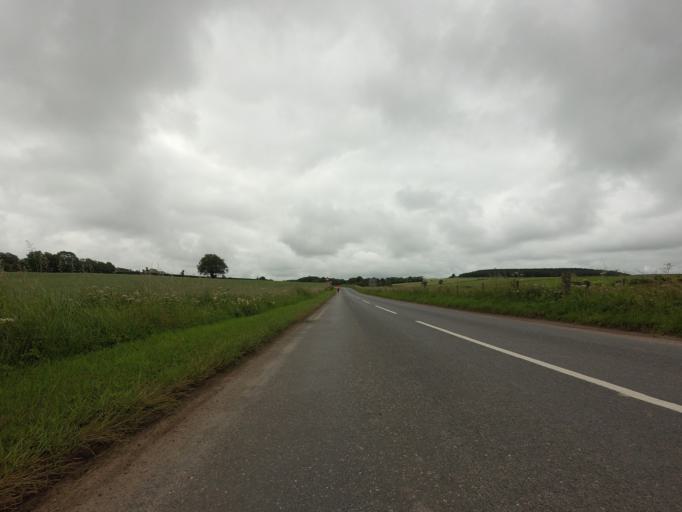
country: GB
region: Scotland
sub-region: Aberdeenshire
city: Turriff
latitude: 57.5451
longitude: -2.3403
